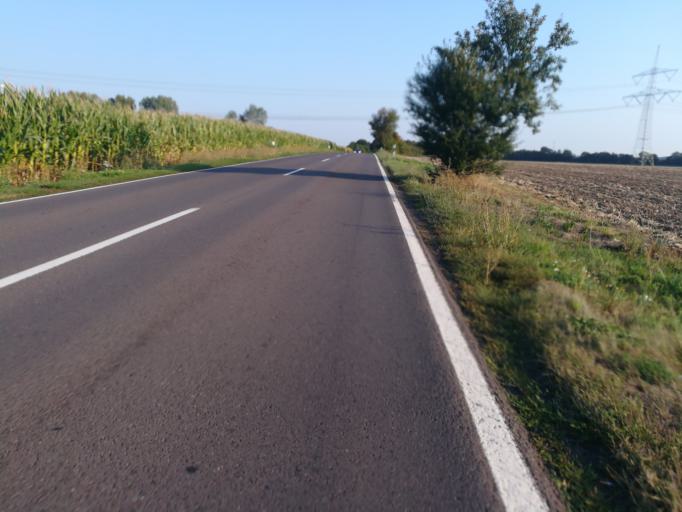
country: DE
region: Saxony-Anhalt
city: Irxleben
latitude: 52.1720
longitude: 11.4756
